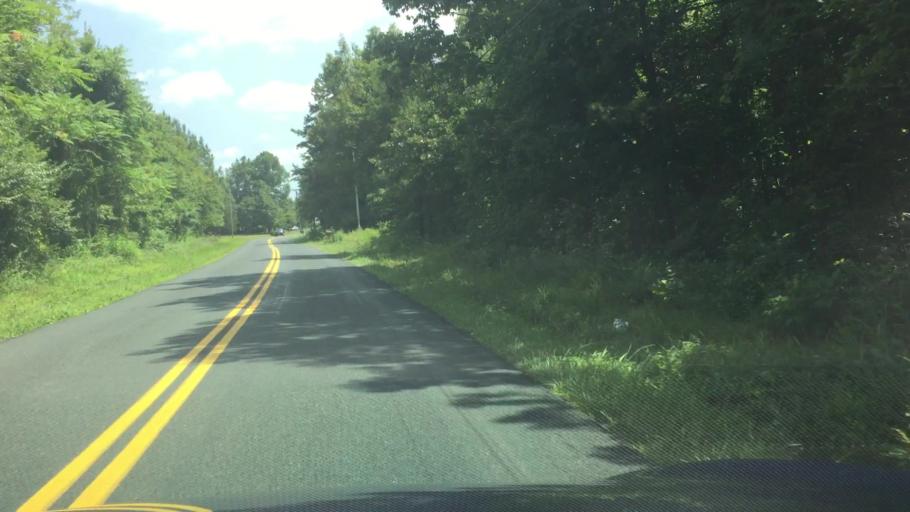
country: US
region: Virginia
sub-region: Appomattox County
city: Appomattox
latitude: 37.3051
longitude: -78.8492
